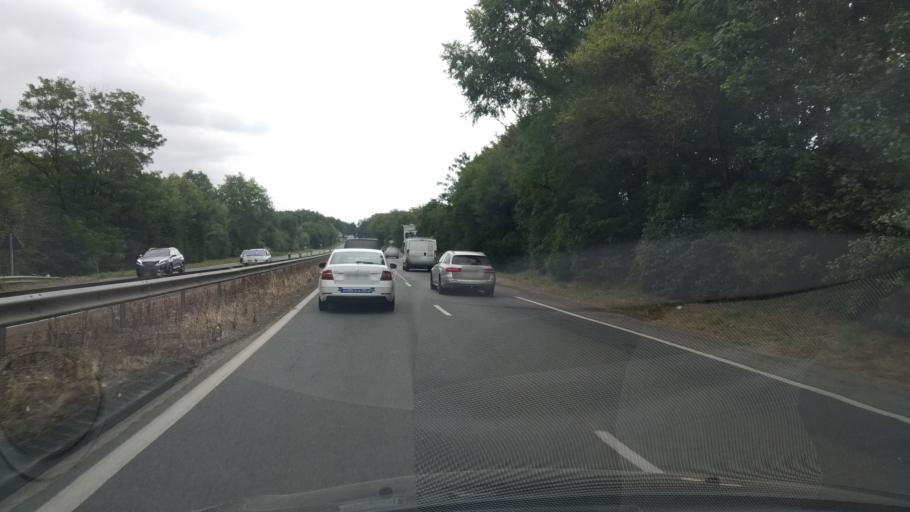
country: FR
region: Poitou-Charentes
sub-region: Departement de la Vienne
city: Biard
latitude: 46.5529
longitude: 0.3112
